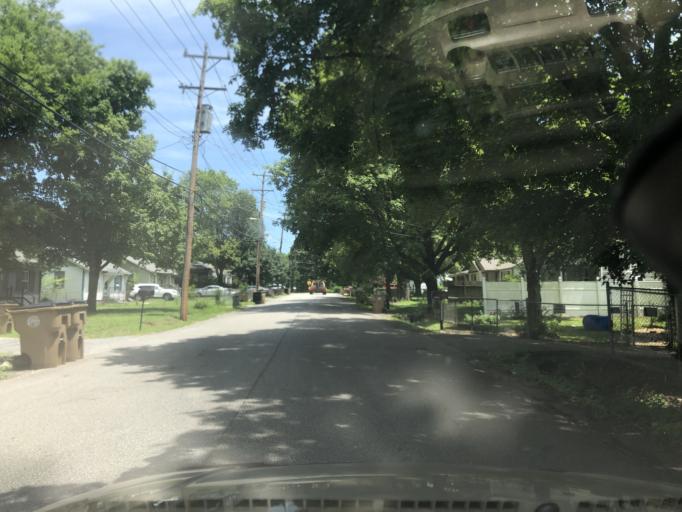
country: US
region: Tennessee
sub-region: Davidson County
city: Goodlettsville
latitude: 36.2596
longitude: -86.7083
